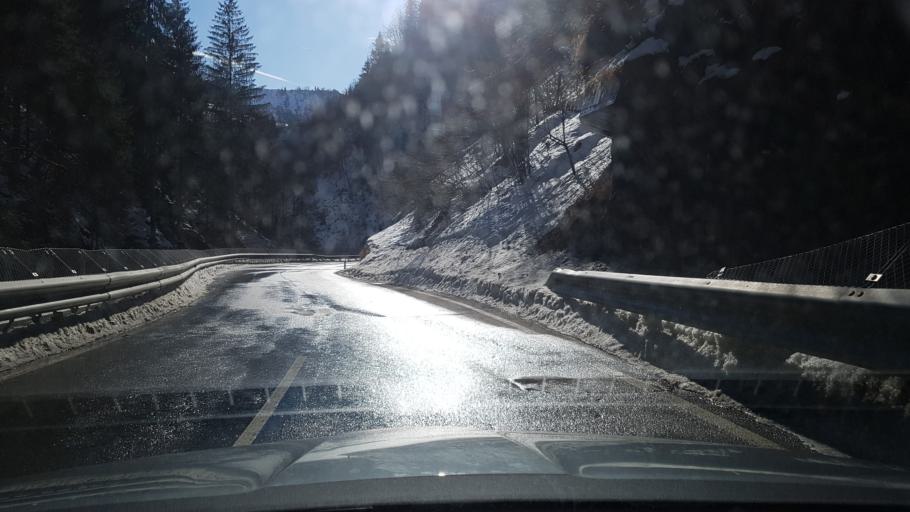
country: AT
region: Salzburg
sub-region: Politischer Bezirk Zell am See
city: Lend
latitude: 47.3206
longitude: 13.0276
